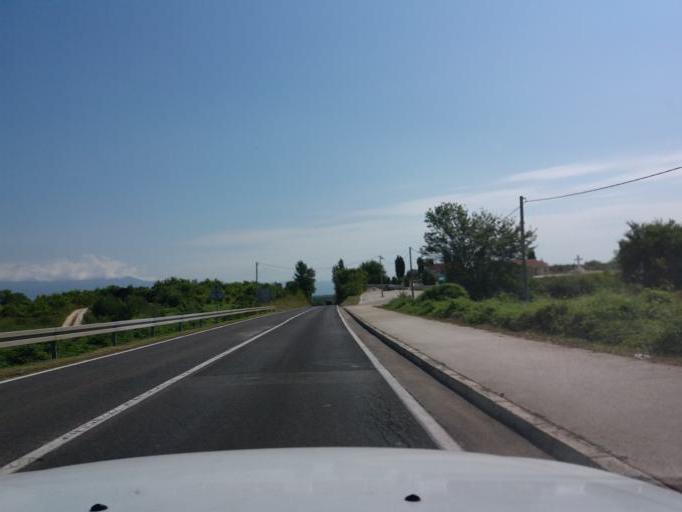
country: HR
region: Zadarska
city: Policnik
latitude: 44.1489
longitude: 15.3277
